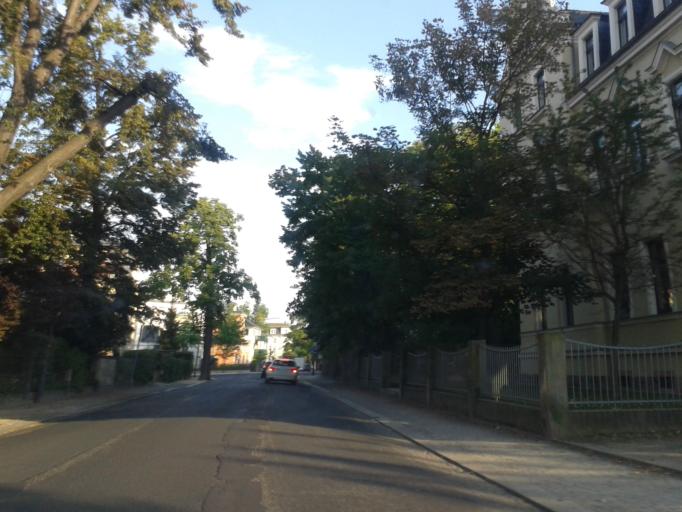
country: DE
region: Saxony
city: Albertstadt
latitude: 51.0479
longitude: 13.8082
